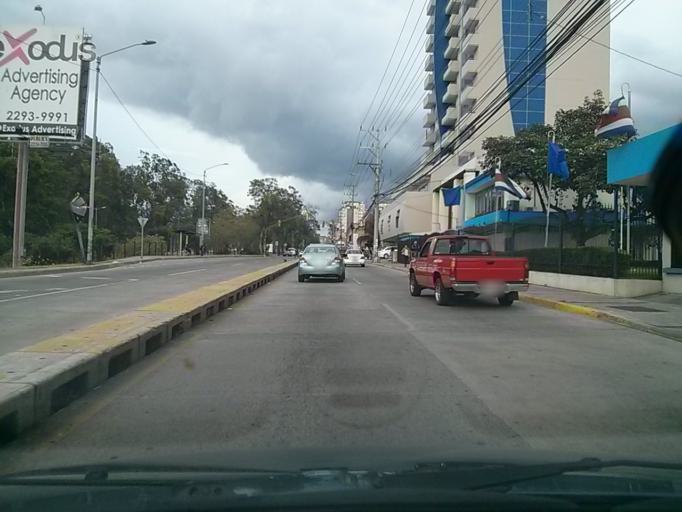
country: CR
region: San Jose
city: San Jose
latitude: 9.9333
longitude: -84.1095
